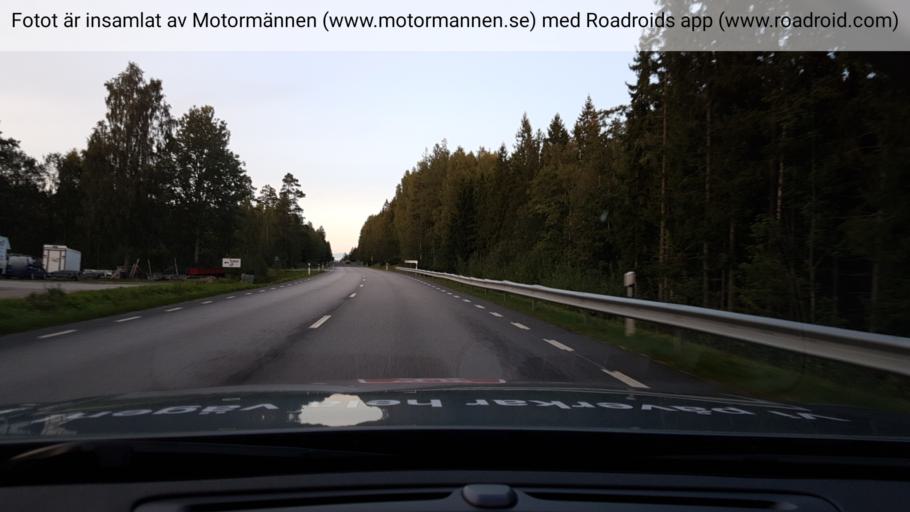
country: SE
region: OErebro
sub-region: Hallefors Kommun
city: Haellefors
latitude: 59.7904
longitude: 14.5407
